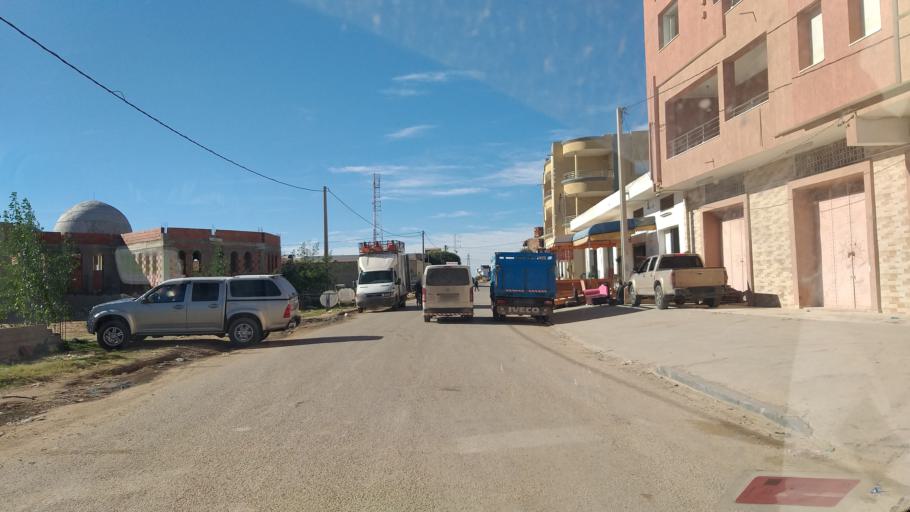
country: TN
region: Al Mahdiyah
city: El Jem
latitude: 35.2921
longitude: 10.6930
